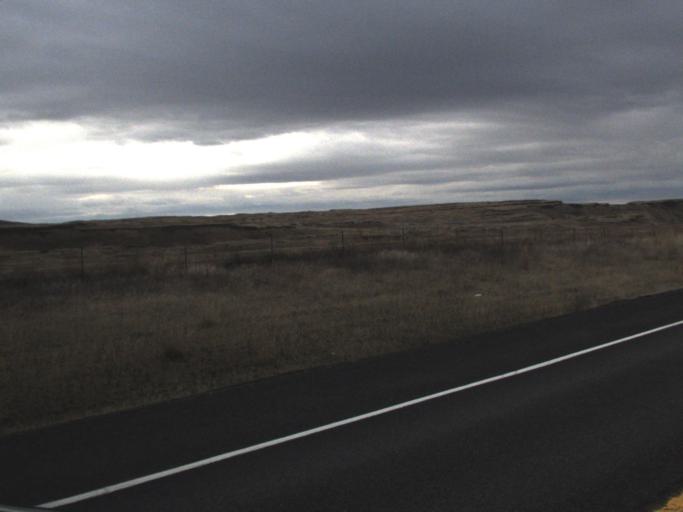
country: US
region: Washington
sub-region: Adams County
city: Ritzville
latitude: 46.7488
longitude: -118.2591
